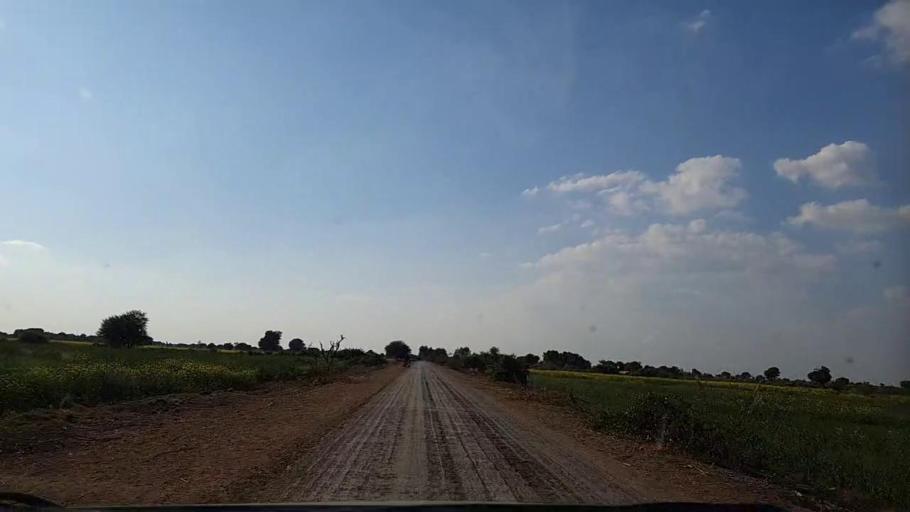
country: PK
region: Sindh
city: Pithoro
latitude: 25.6491
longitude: 69.2983
